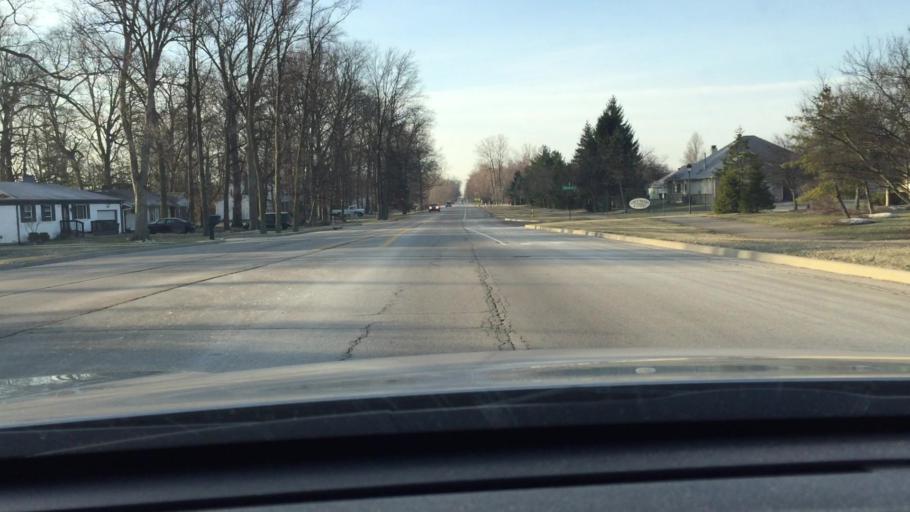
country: US
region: Indiana
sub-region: Hamilton County
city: Carmel
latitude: 39.9555
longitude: -86.1460
